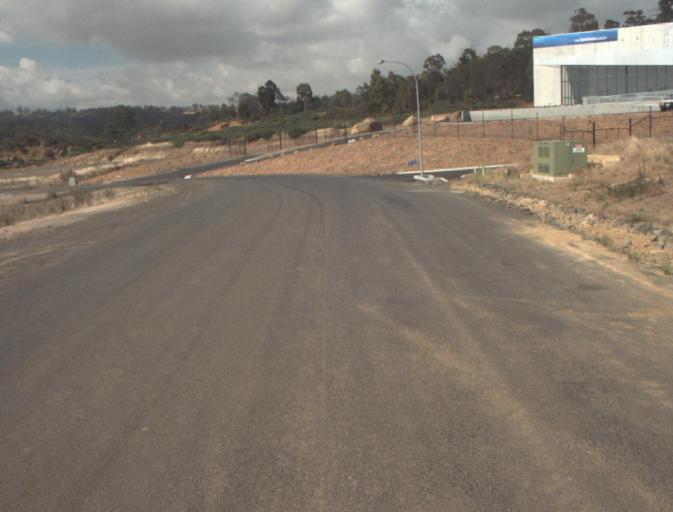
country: AU
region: Tasmania
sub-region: Launceston
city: Summerhill
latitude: -41.4787
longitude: 147.1511
